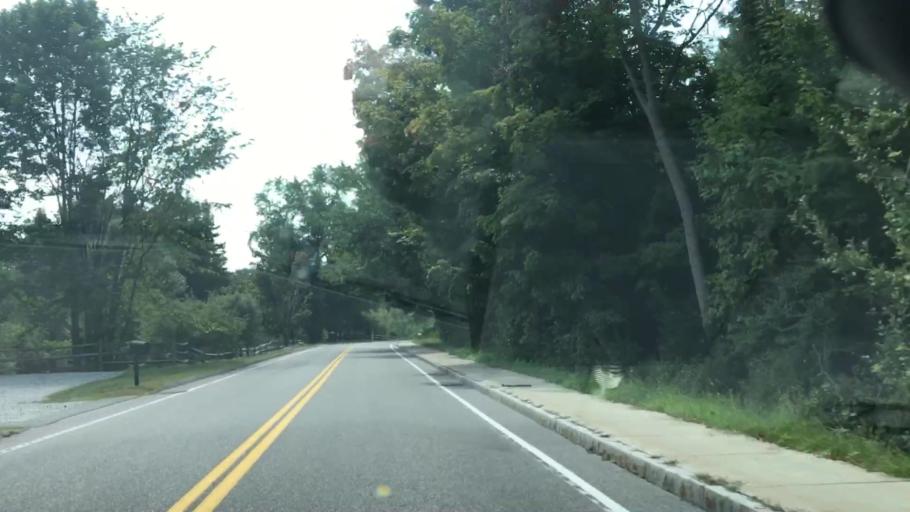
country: US
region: New Hampshire
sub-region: Hillsborough County
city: Bedford
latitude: 42.9453
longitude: -71.5187
